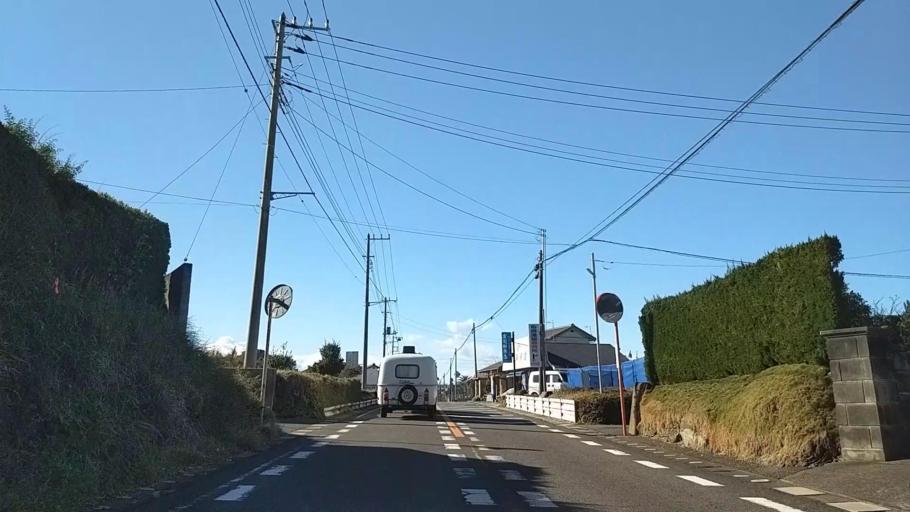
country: JP
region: Chiba
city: Tateyama
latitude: 34.9263
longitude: 139.8343
